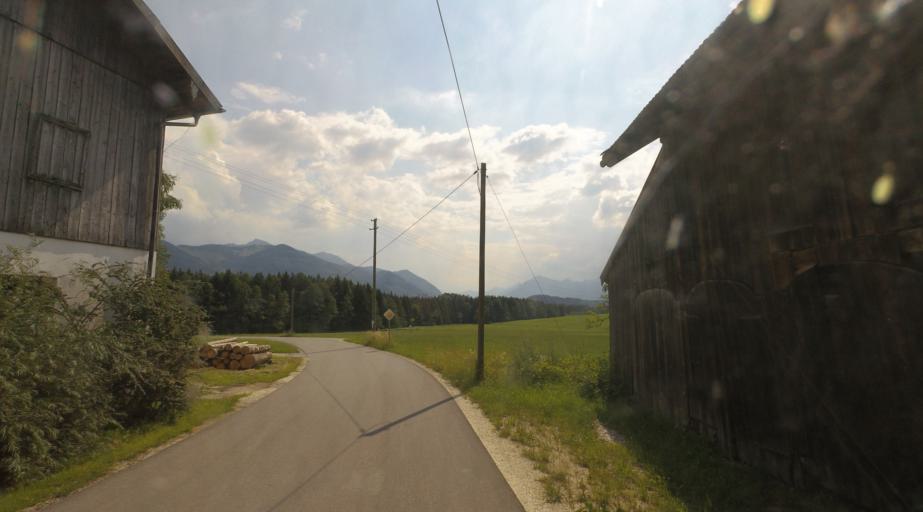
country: DE
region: Bavaria
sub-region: Upper Bavaria
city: Grabenstatt
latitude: 47.8188
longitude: 12.5509
